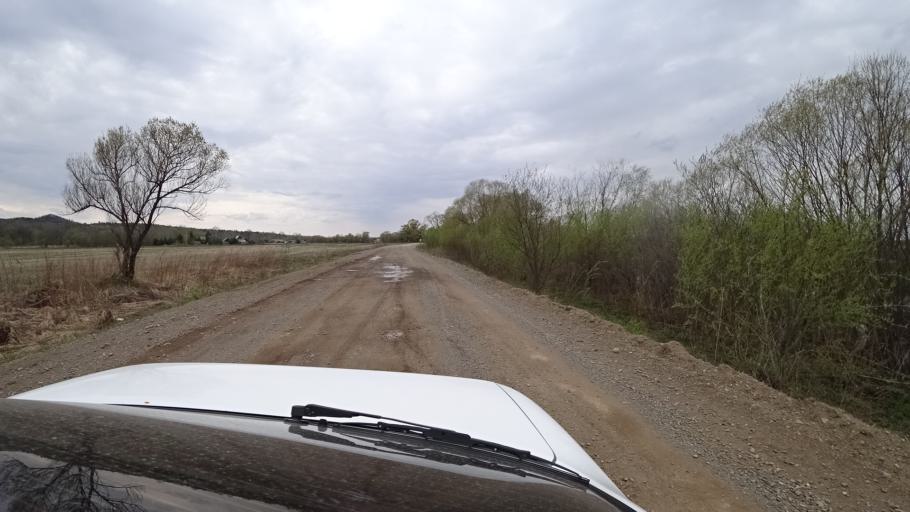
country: RU
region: Primorskiy
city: Novopokrovka
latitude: 45.4910
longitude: 134.4559
